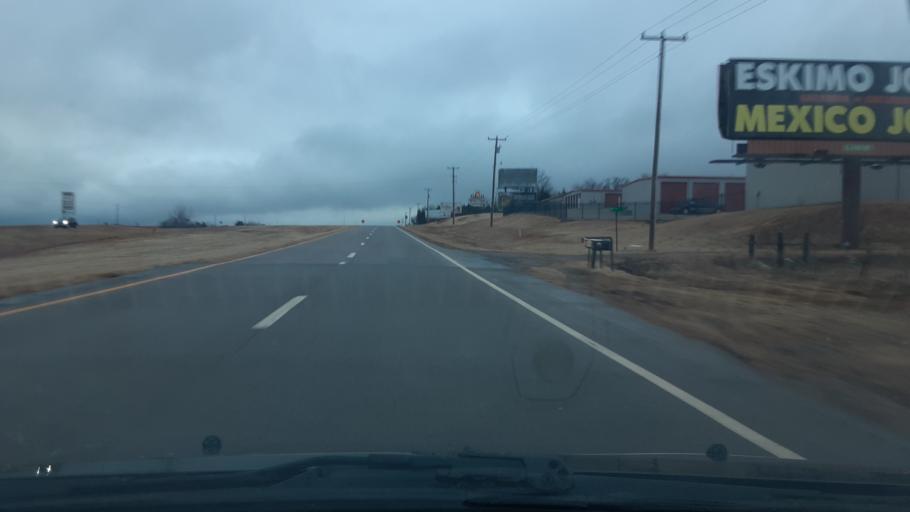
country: US
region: Oklahoma
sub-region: Payne County
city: Stillwater
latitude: 36.1159
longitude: -97.1701
